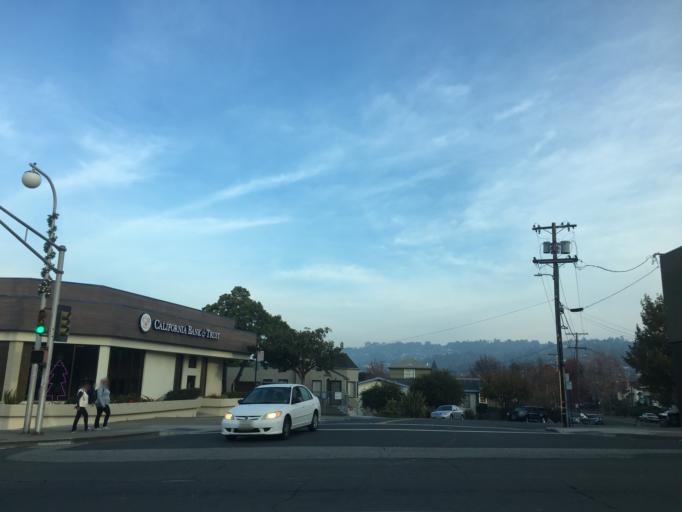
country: US
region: California
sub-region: Alameda County
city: Albany
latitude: 37.8907
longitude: -122.2887
